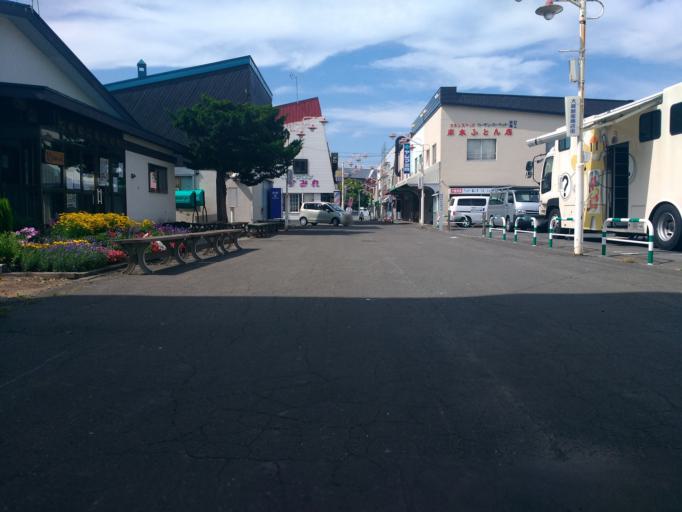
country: JP
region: Hokkaido
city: Ebetsu
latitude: 43.0794
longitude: 141.4984
